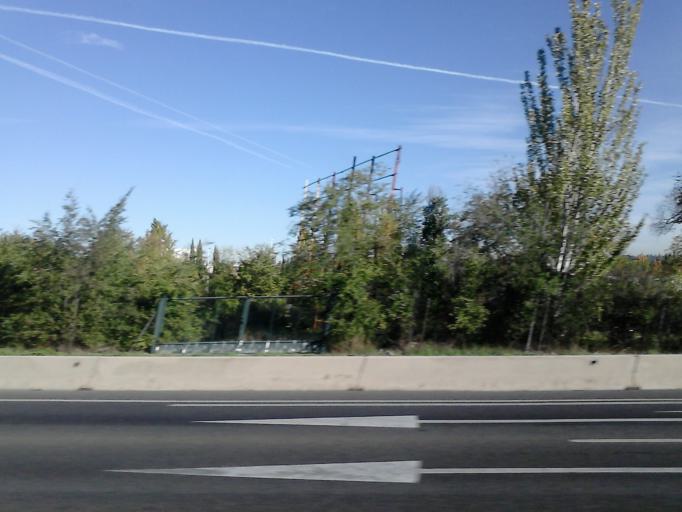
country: ES
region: Madrid
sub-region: Provincia de Madrid
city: Moncloa-Aravaca
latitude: 40.4619
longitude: -3.7675
